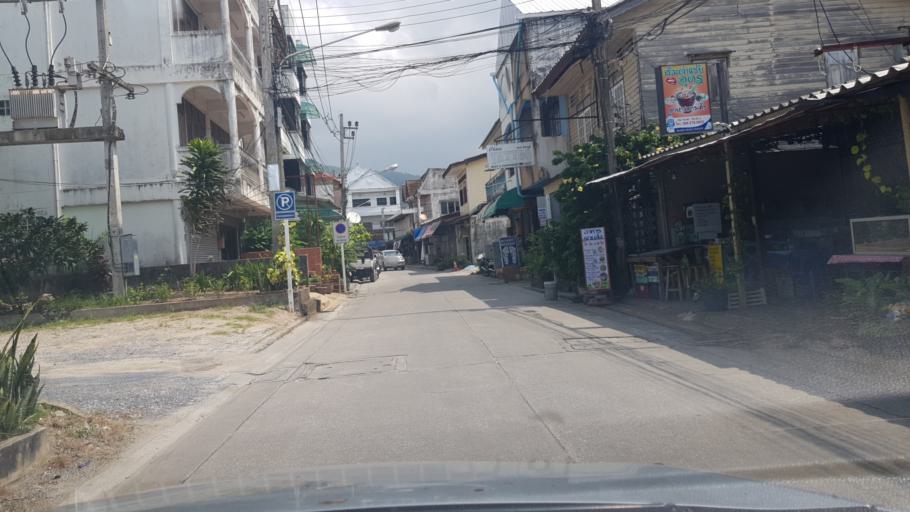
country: TH
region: Surat Thani
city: Ko Samui
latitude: 9.5322
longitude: 99.9349
